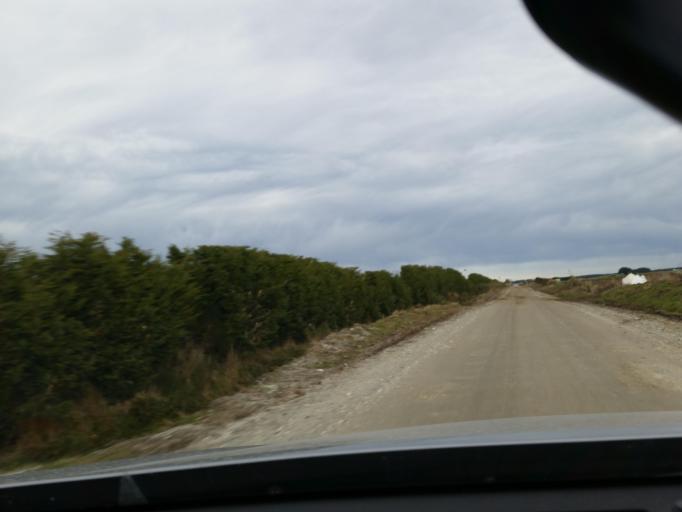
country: NZ
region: Southland
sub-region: Invercargill City
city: Invercargill
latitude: -46.4376
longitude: 168.5062
